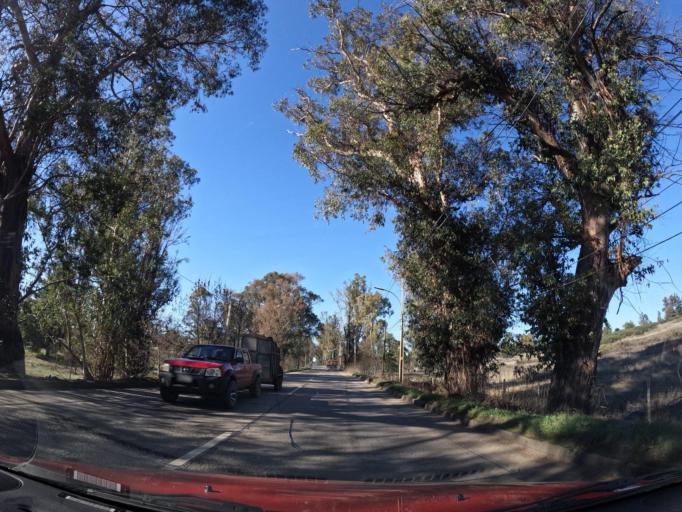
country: CL
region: Maule
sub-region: Provincia de Cauquenes
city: Cauquenes
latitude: -35.9580
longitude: -72.2903
